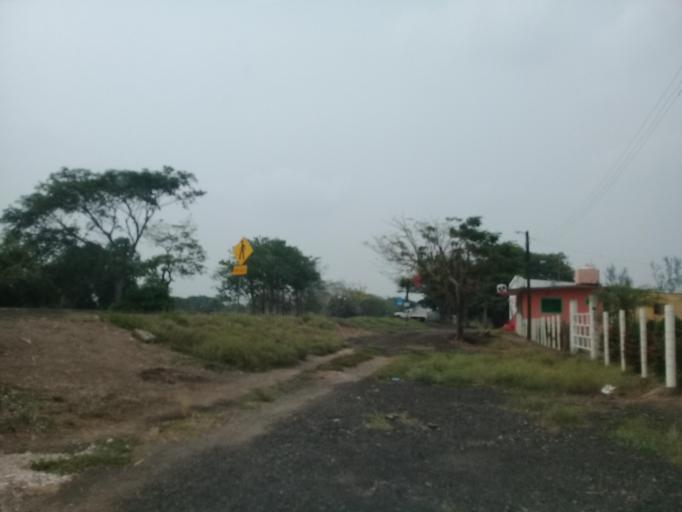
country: MX
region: Veracruz
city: Jamapa
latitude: 18.9458
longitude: -96.1979
